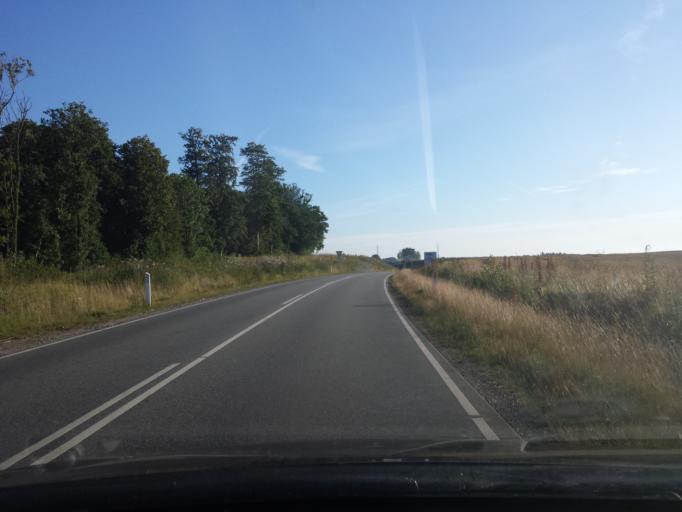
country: DK
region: South Denmark
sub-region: Sonderborg Kommune
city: Grasten
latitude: 54.9487
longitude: 9.6348
